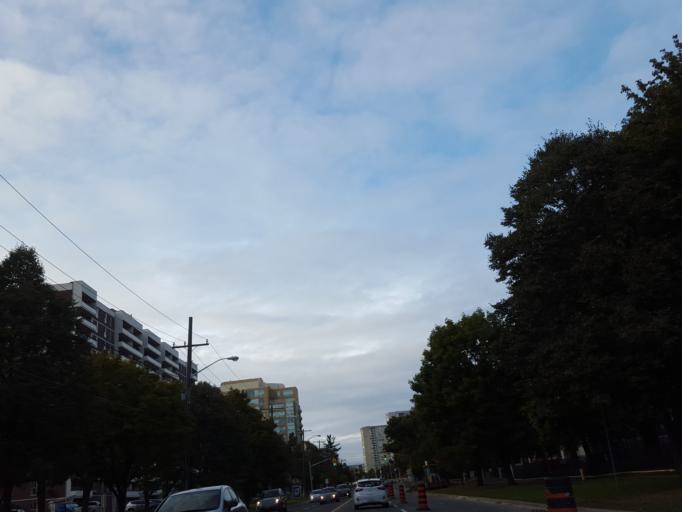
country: CA
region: Ontario
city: Scarborough
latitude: 43.7936
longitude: -79.3145
